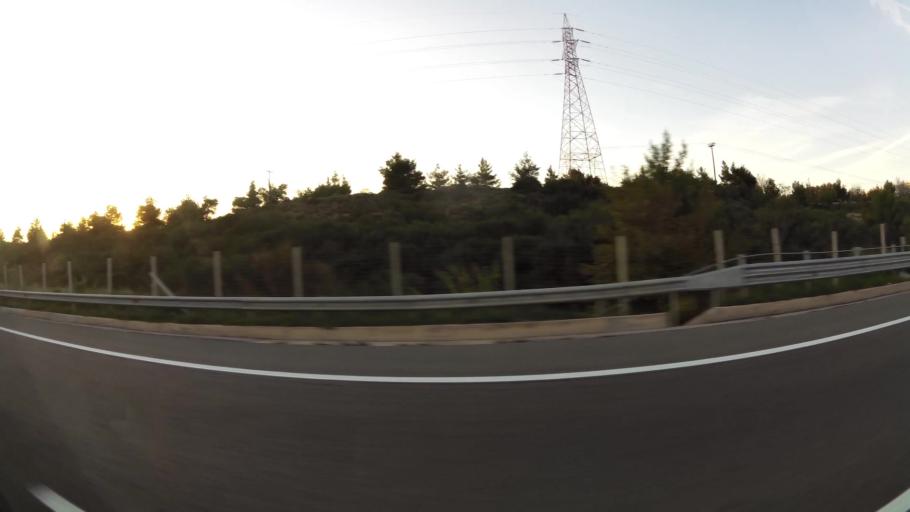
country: GR
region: Attica
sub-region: Nomarchia Athinas
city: Ekali
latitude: 38.1231
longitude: 23.8348
